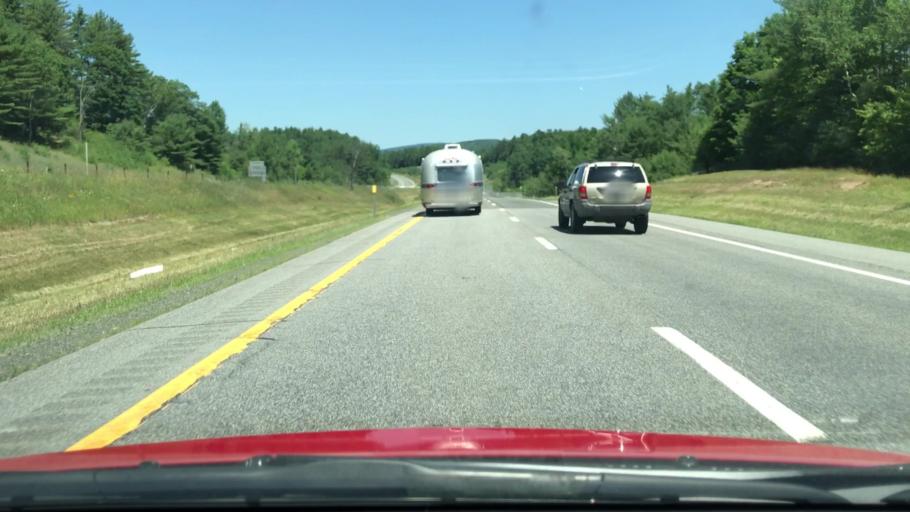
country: US
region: New York
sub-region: Essex County
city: Elizabethtown
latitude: 44.3040
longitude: -73.5305
